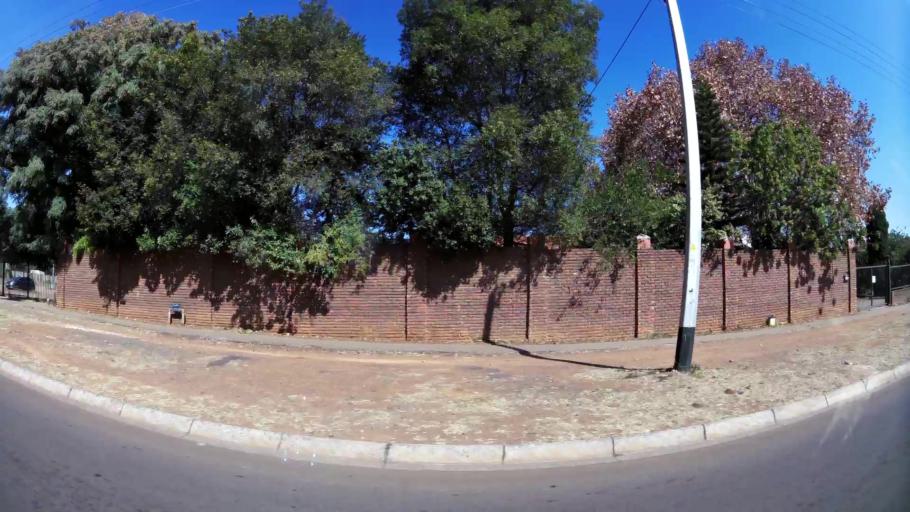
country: ZA
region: Gauteng
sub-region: City of Tshwane Metropolitan Municipality
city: Pretoria
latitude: -25.7569
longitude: 28.2321
